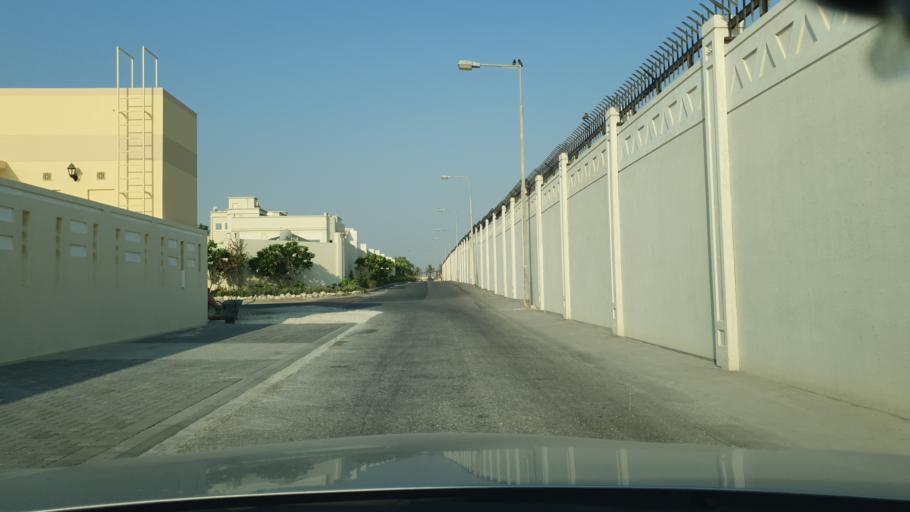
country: BH
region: Northern
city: Madinat `Isa
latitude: 26.1547
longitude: 50.5395
